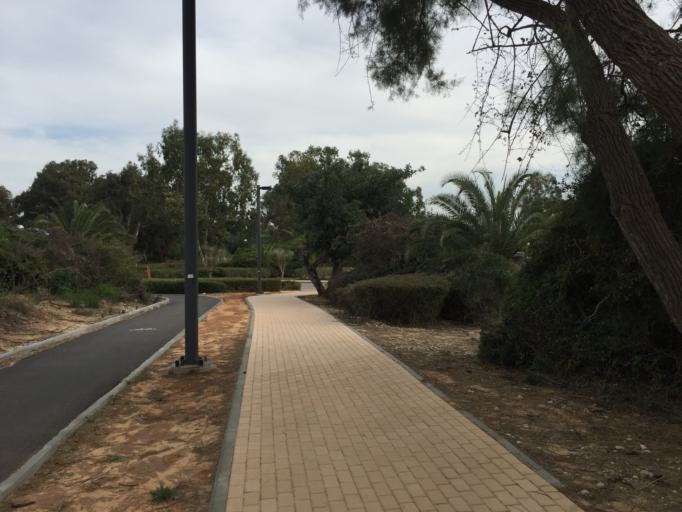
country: IL
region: Haifa
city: Qesarya
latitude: 32.5047
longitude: 34.9045
